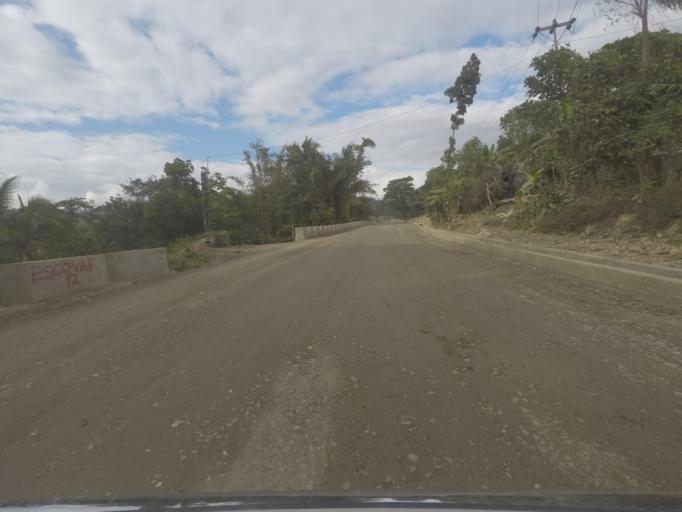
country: TL
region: Baucau
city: Venilale
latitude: -8.6277
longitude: 126.3834
